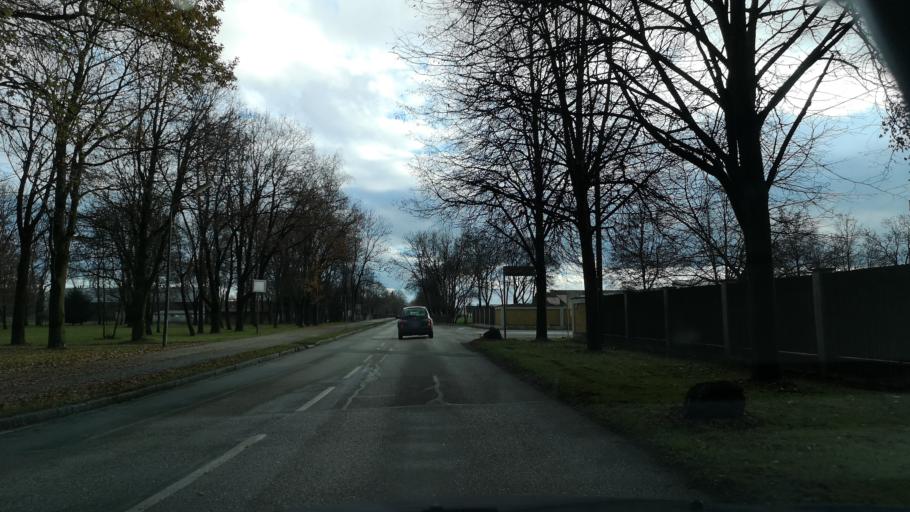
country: DE
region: Bavaria
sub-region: Upper Bavaria
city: Kirchheim bei Muenchen
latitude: 48.1705
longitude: 11.7791
